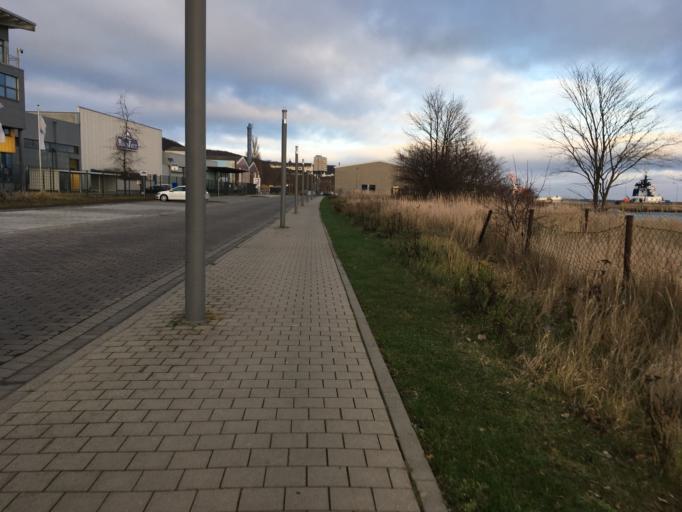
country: DE
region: Mecklenburg-Vorpommern
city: Sassnitz
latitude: 54.5077
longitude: 13.6317
